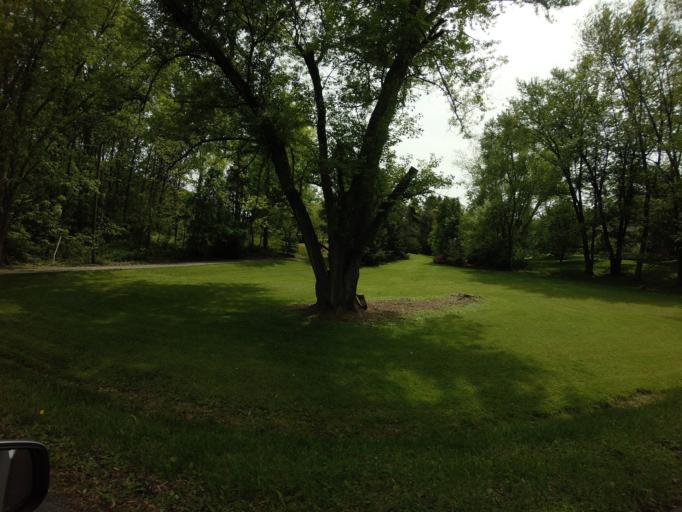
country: US
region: Maryland
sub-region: Carroll County
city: Westminster
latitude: 39.4767
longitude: -77.0262
